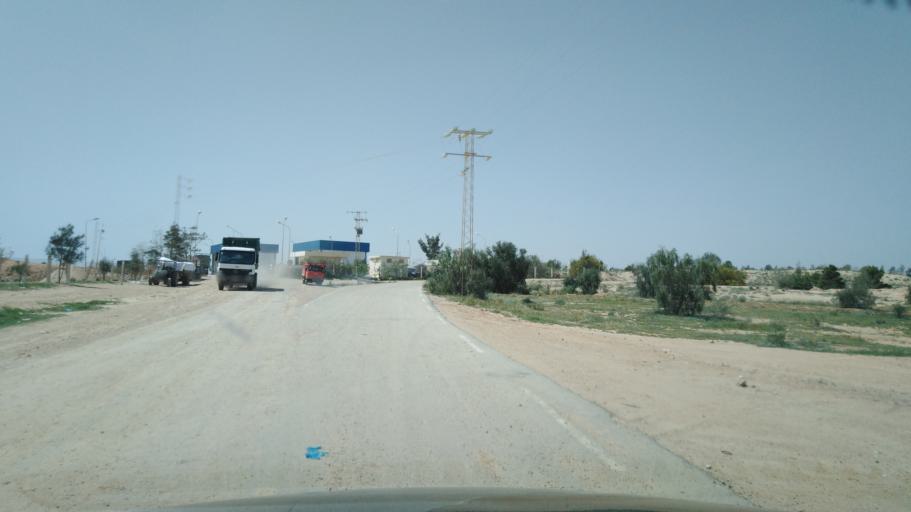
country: TN
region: Safaqis
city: Sfax
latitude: 34.7101
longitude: 10.5254
